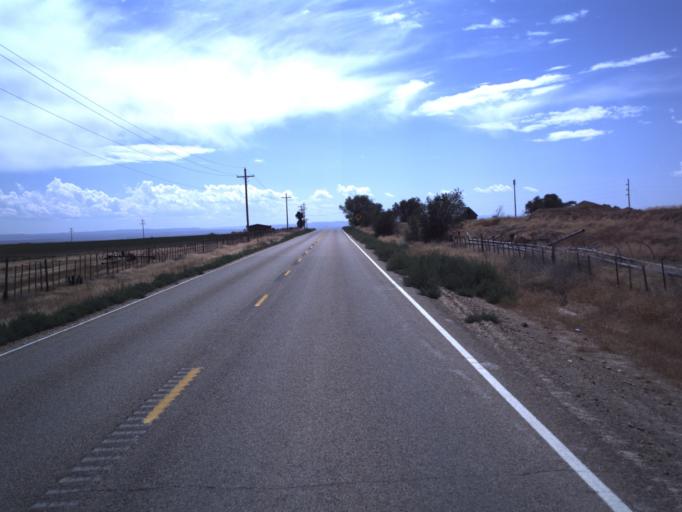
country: US
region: Utah
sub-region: Uintah County
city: Maeser
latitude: 40.2281
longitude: -109.6844
